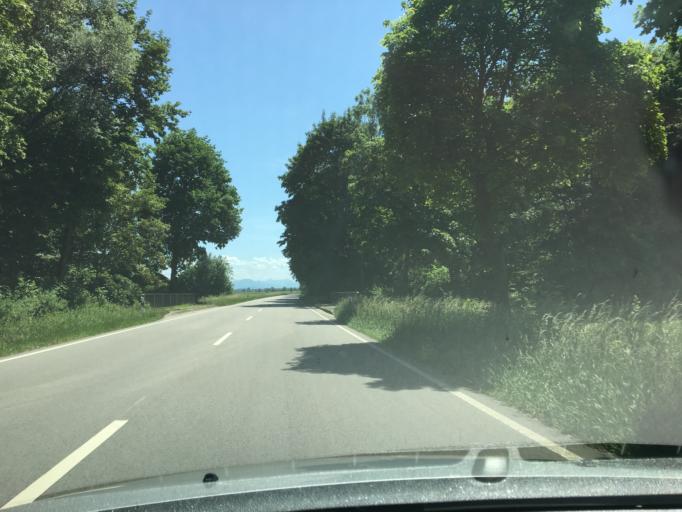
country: DE
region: Bavaria
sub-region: Upper Bavaria
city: Tittmoning
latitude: 48.0444
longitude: 12.7827
